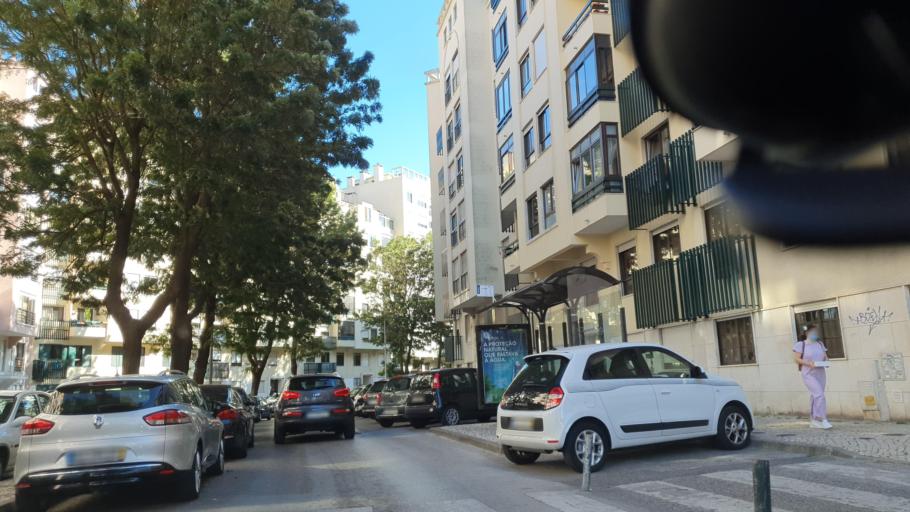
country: PT
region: Lisbon
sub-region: Sintra
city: Queluz
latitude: 38.7566
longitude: -9.2774
